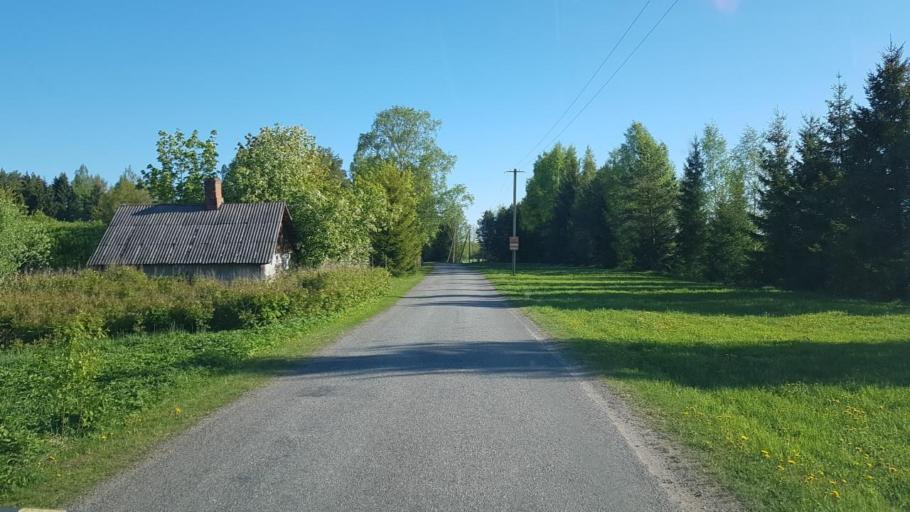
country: EE
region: Laeaene-Virumaa
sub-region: Viru-Nigula vald
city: Kunda
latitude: 59.3282
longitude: 26.6362
